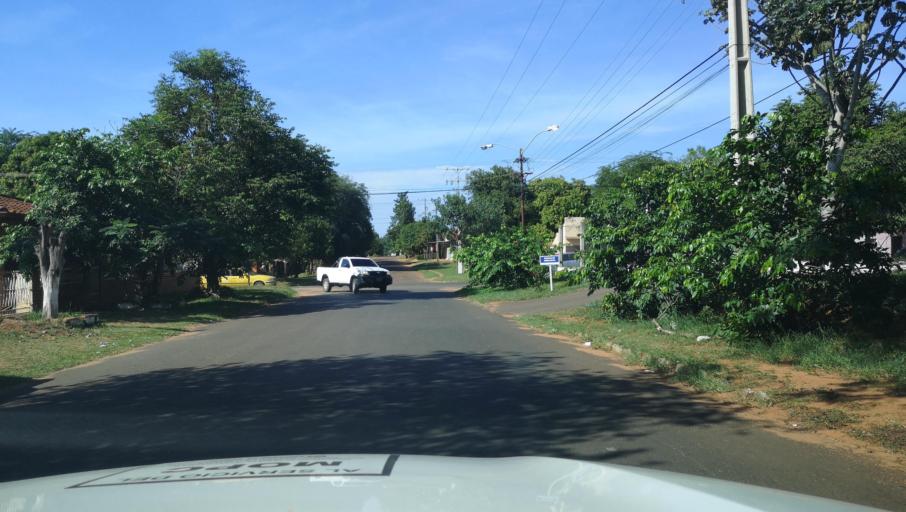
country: PY
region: Misiones
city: Santa Maria
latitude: -26.8903
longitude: -57.0174
